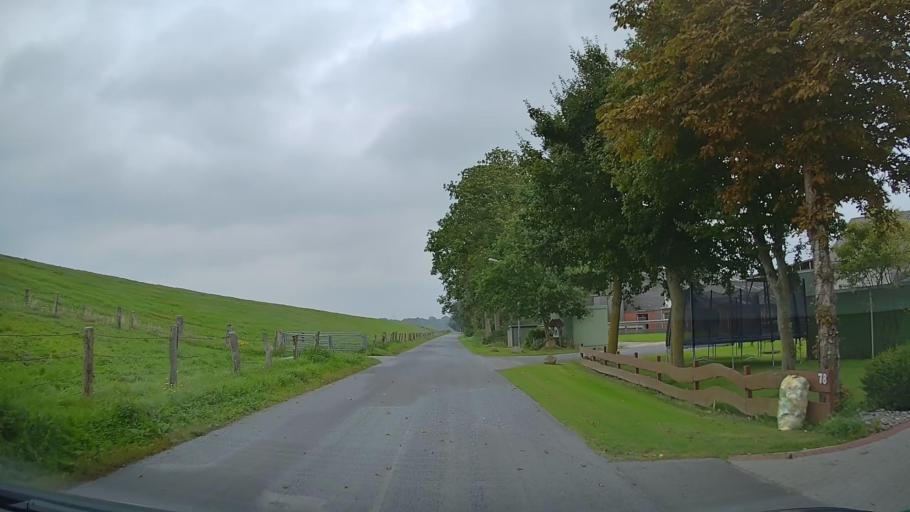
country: DE
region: Lower Saxony
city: Belum
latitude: 53.8229
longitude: 9.0134
